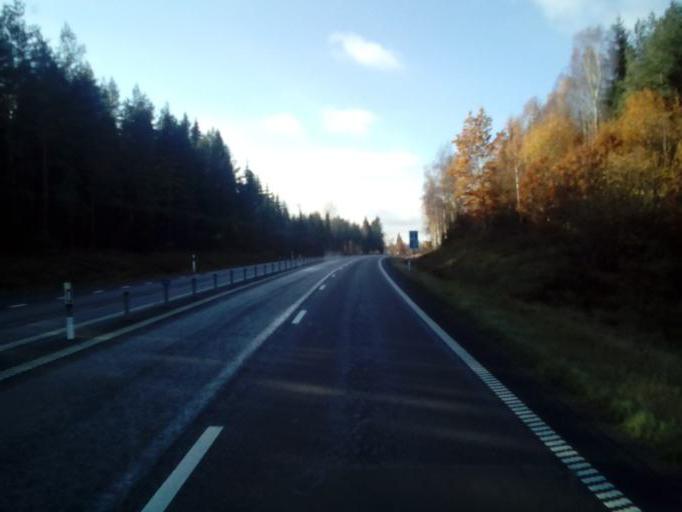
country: SE
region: Kalmar
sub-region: Vimmerby Kommun
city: Vimmerby
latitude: 57.6855
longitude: 15.9962
